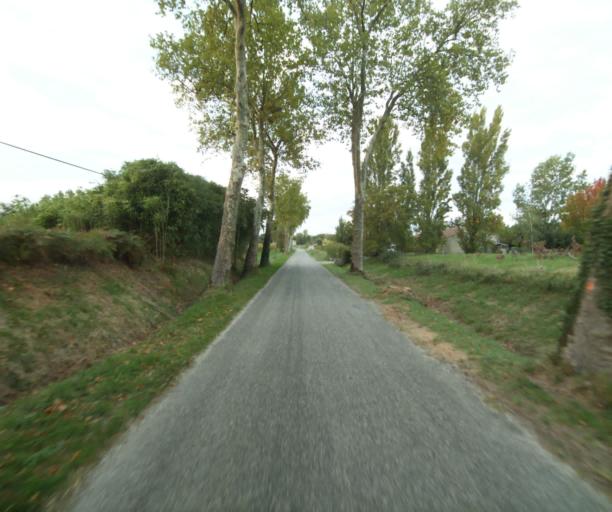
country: FR
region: Aquitaine
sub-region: Departement des Landes
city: Gabarret
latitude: 43.9760
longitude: 0.0933
